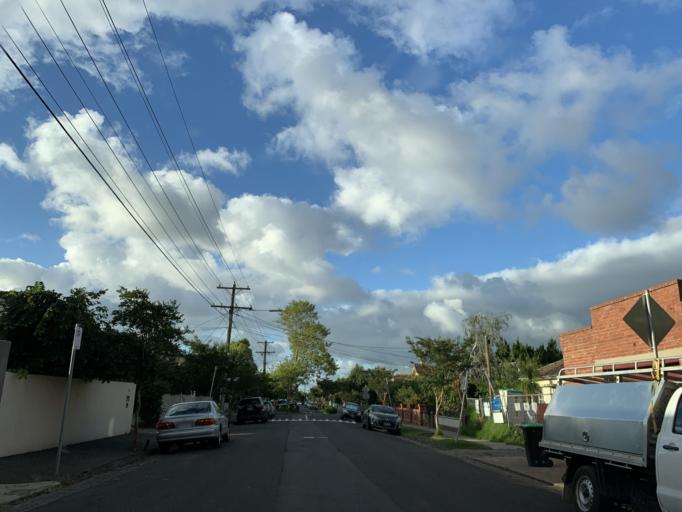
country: AU
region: Victoria
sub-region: Moonee Valley
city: Moonee Ponds
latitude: -37.7638
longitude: 144.9157
